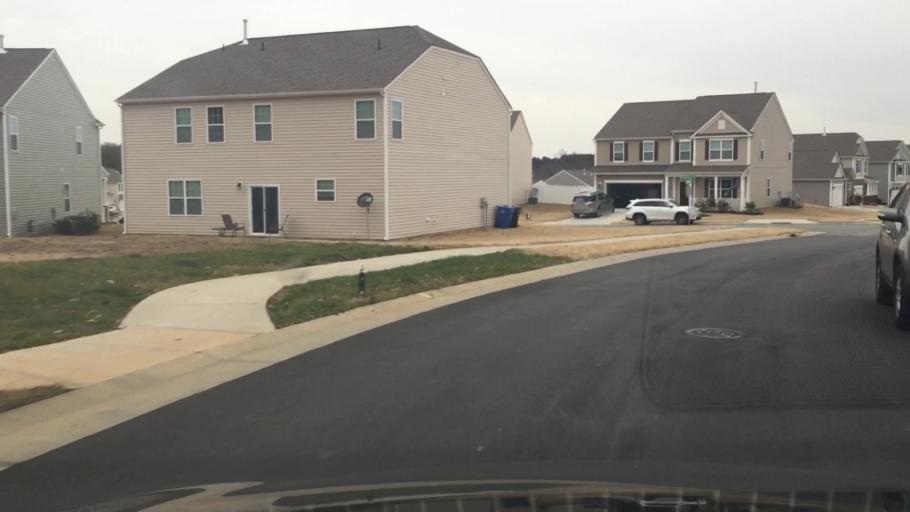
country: US
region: North Carolina
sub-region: Iredell County
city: Mooresville
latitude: 35.5806
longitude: -80.7943
